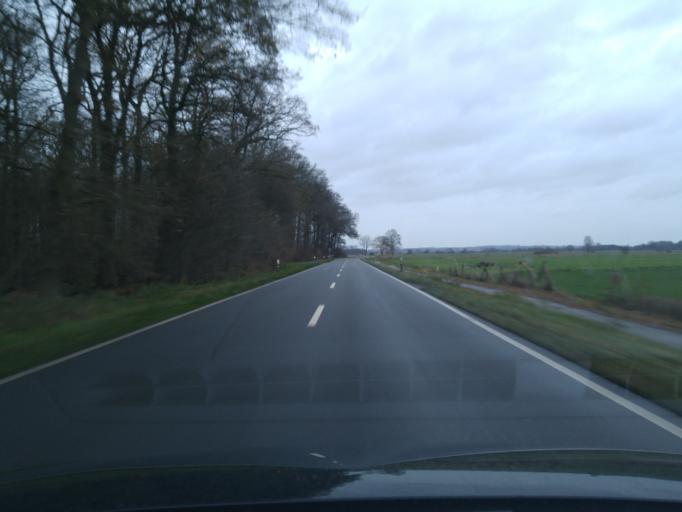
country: DE
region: Lower Saxony
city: Scharnebeck
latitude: 53.3116
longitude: 10.5071
